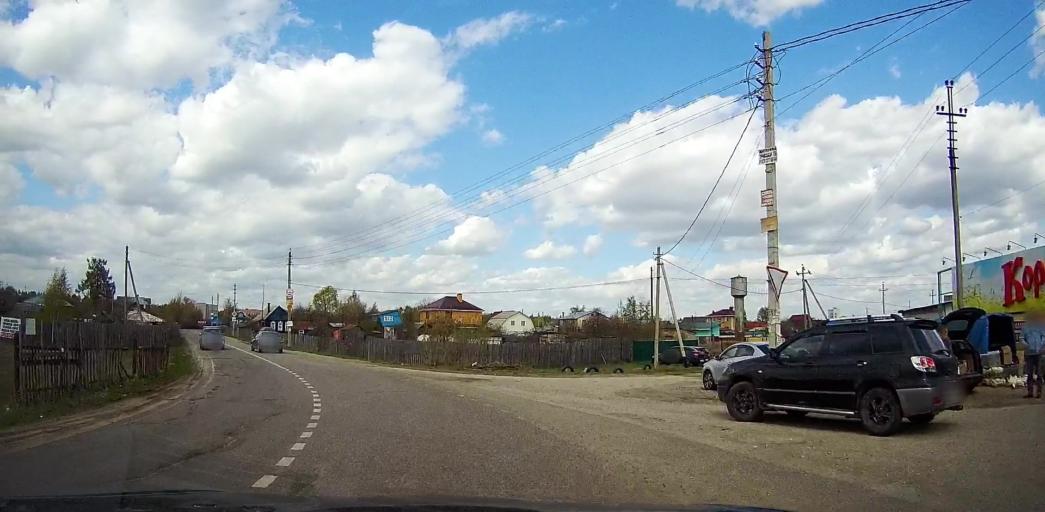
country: RU
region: Moskovskaya
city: Davydovo
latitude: 55.6039
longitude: 38.8464
